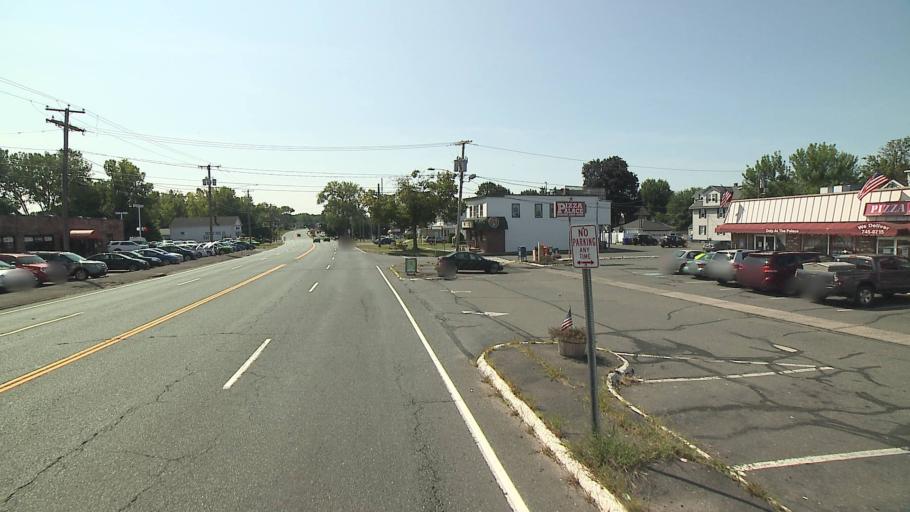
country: US
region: Connecticut
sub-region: Hartford County
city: Thompsonville
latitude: 42.0102
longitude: -72.5936
